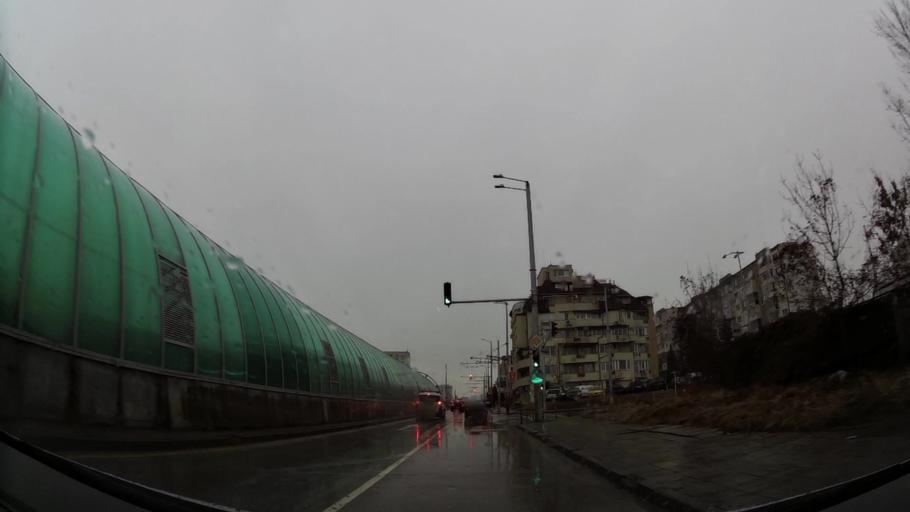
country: BG
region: Sofia-Capital
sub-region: Stolichna Obshtina
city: Sofia
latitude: 42.6552
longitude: 23.3700
